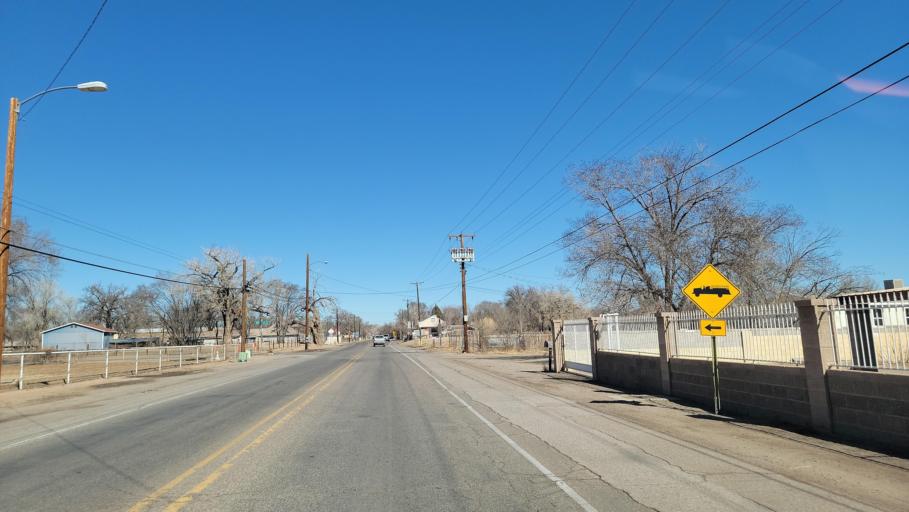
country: US
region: New Mexico
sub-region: Bernalillo County
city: South Valley
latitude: 34.9916
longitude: -106.6949
